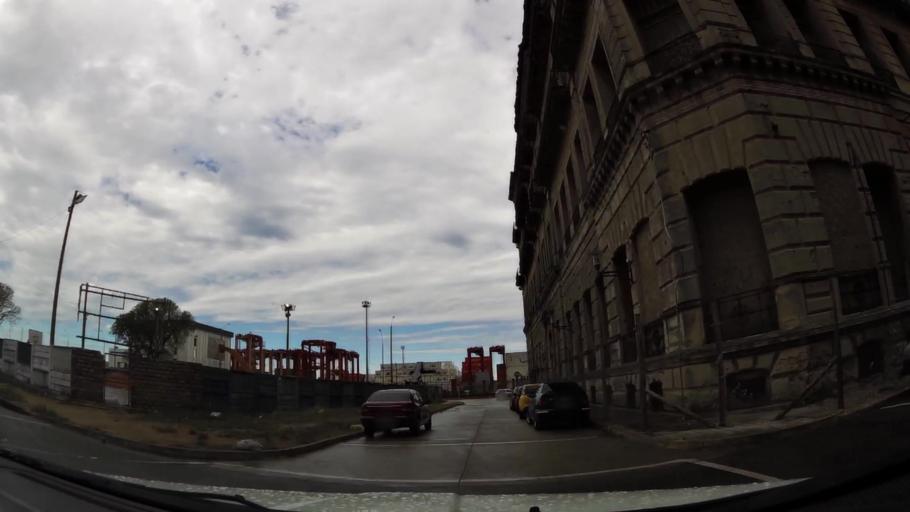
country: UY
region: Montevideo
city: Montevideo
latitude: -34.9077
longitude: -56.2140
